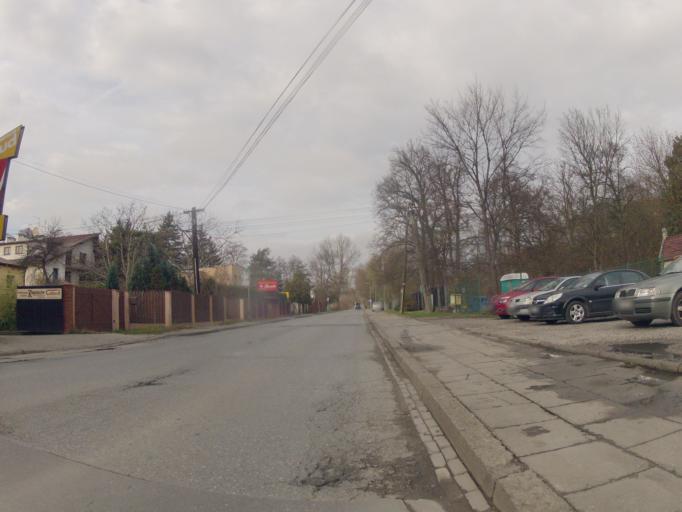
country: PL
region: Lesser Poland Voivodeship
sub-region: Powiat krakowski
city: Rzaska
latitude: 50.0866
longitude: 19.8421
